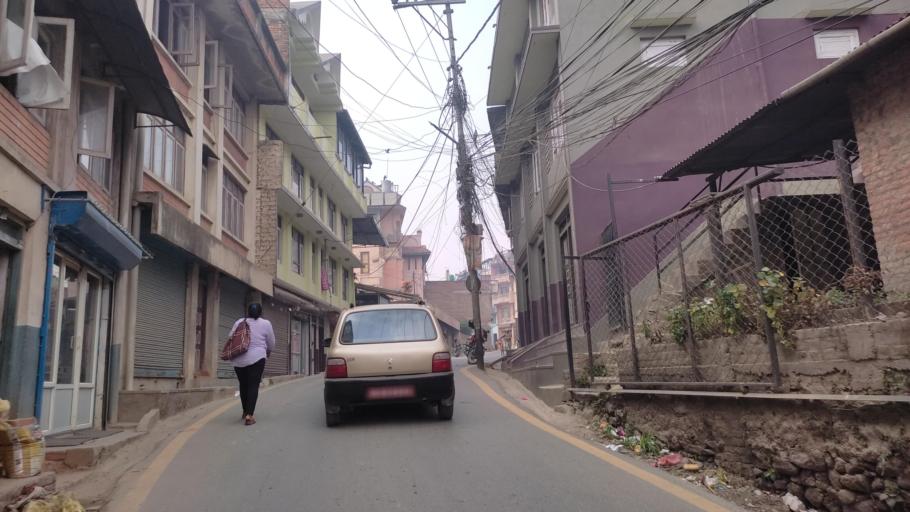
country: NP
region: Central Region
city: Kirtipur
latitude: 27.6794
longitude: 85.2727
